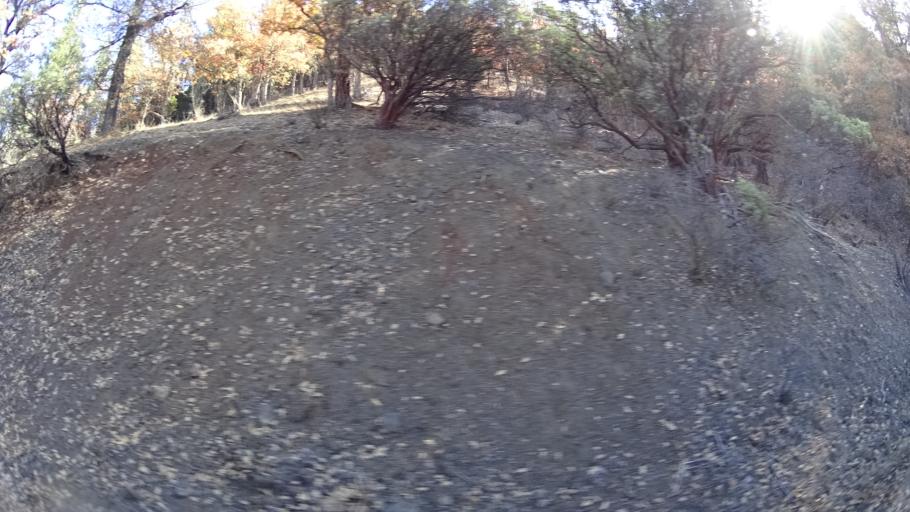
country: US
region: California
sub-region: Siskiyou County
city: Yreka
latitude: 41.8579
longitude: -122.8257
